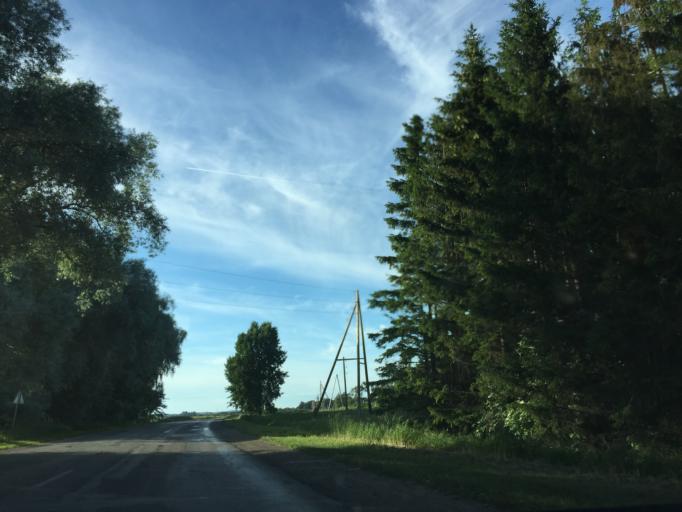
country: LV
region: Ventspils
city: Ventspils
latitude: 57.3069
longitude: 21.5575
